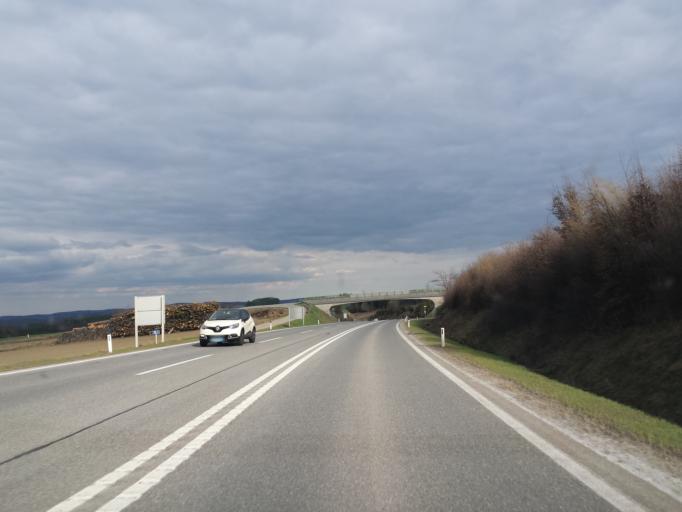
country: AT
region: Lower Austria
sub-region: Politischer Bezirk Krems
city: Krumau am Kamp
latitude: 48.5371
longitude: 15.3891
